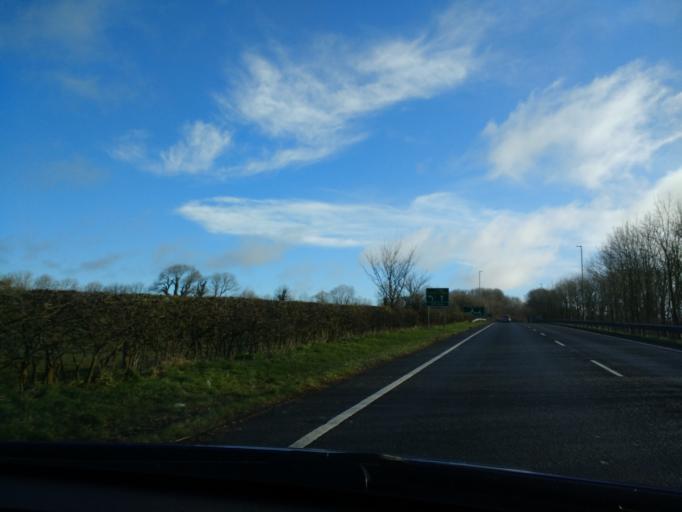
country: GB
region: England
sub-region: Cumbria
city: Cockermouth
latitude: 54.6729
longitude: -3.3820
